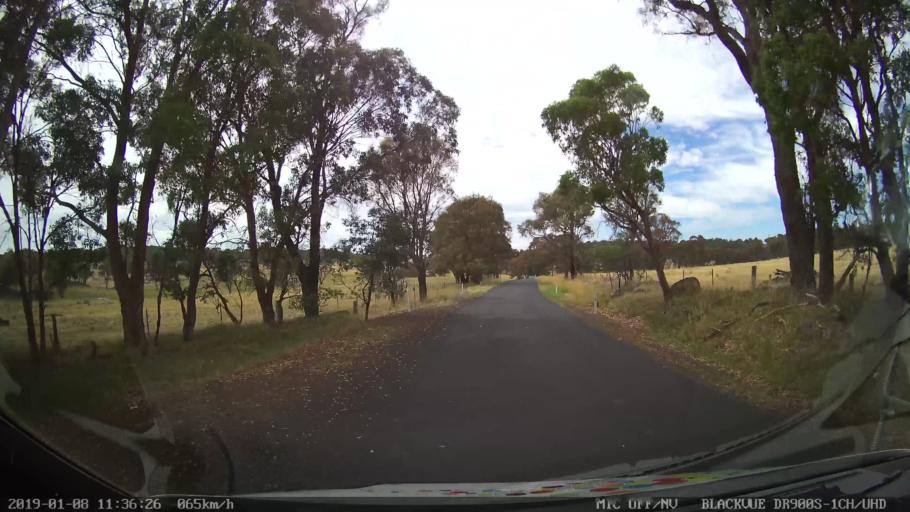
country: AU
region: New South Wales
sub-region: Guyra
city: Guyra
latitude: -30.3454
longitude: 151.5439
